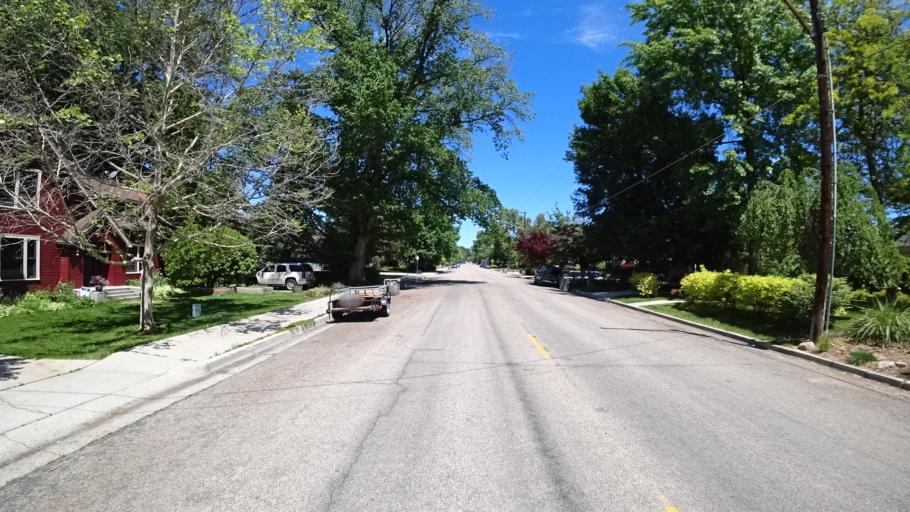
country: US
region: Idaho
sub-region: Ada County
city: Boise
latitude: 43.5950
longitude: -116.2236
